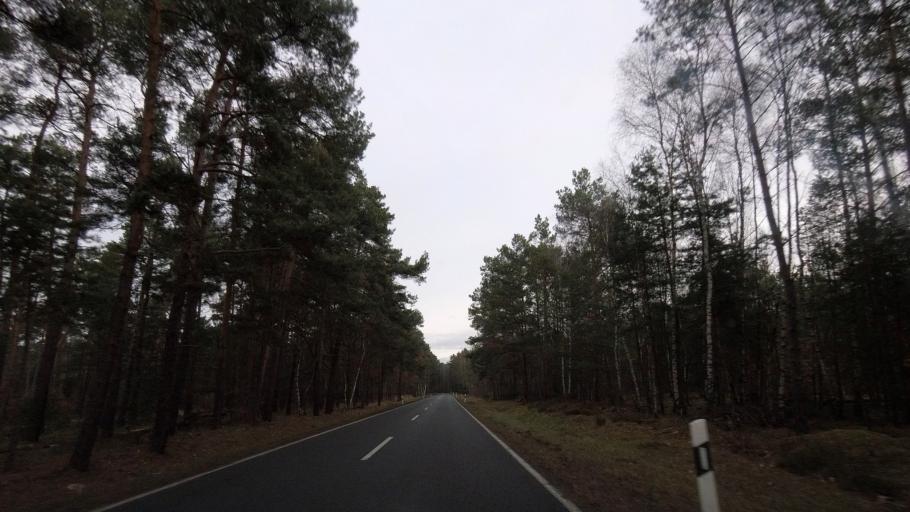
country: DE
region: Brandenburg
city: Niedergorsdorf
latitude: 52.0224
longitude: 12.9481
